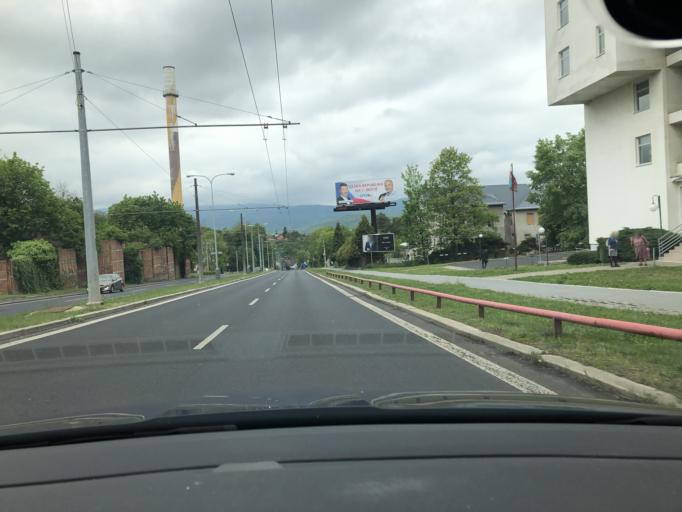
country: CZ
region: Ustecky
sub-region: Okres Usti nad Labem
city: Usti nad Labem
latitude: 50.6808
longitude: 14.0223
